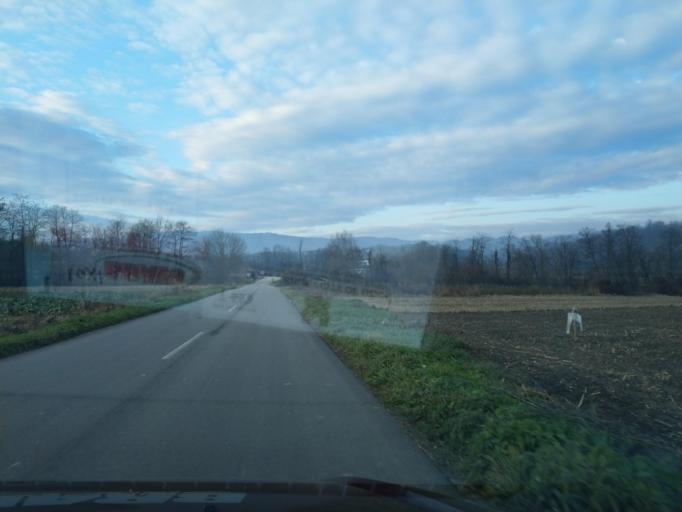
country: RS
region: Central Serbia
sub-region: Zlatiborski Okrug
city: Kosjeric
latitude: 43.9227
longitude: 19.9015
